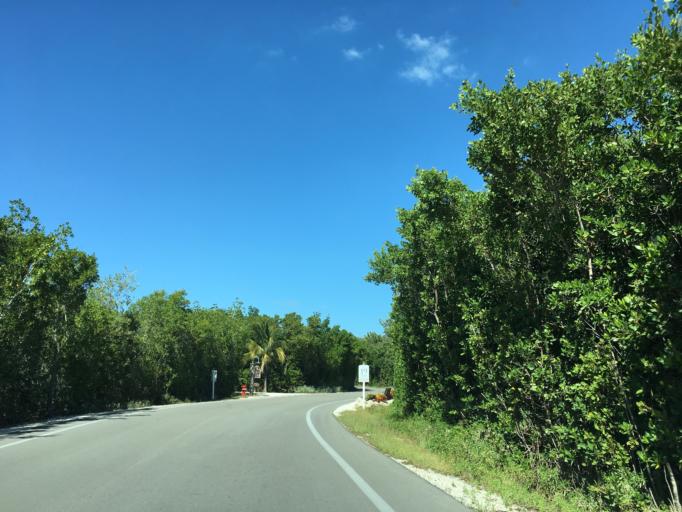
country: US
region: Florida
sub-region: Lee County
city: Pine Island Center
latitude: 26.5307
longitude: -82.1935
